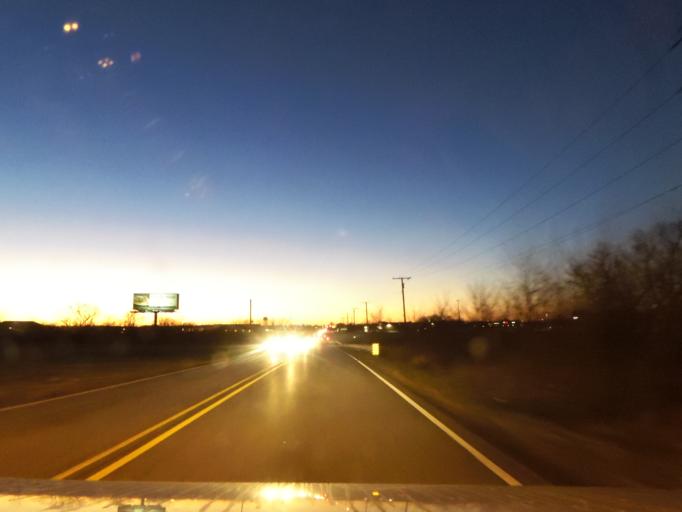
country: US
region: Indiana
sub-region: Lake County
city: Crown Point
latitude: 41.4202
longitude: -87.3300
